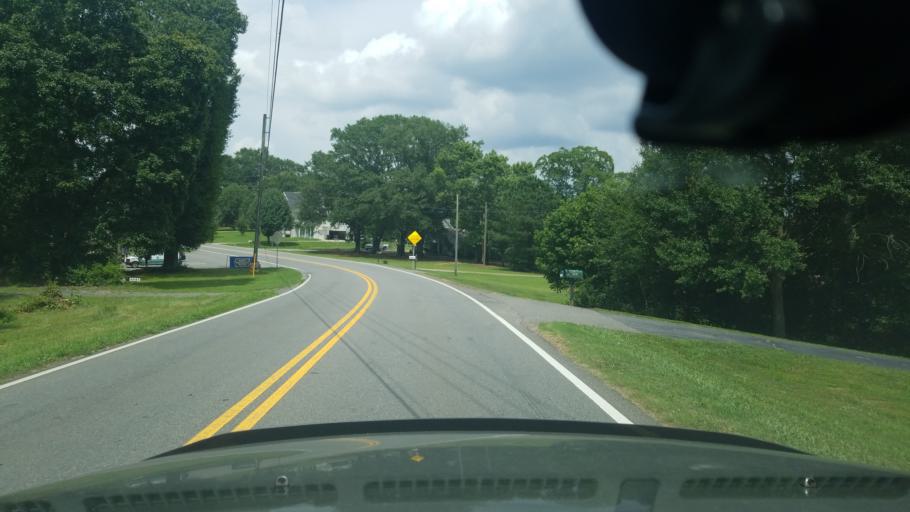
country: US
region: Georgia
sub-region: Forsyth County
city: Cumming
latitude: 34.2665
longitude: -84.2364
